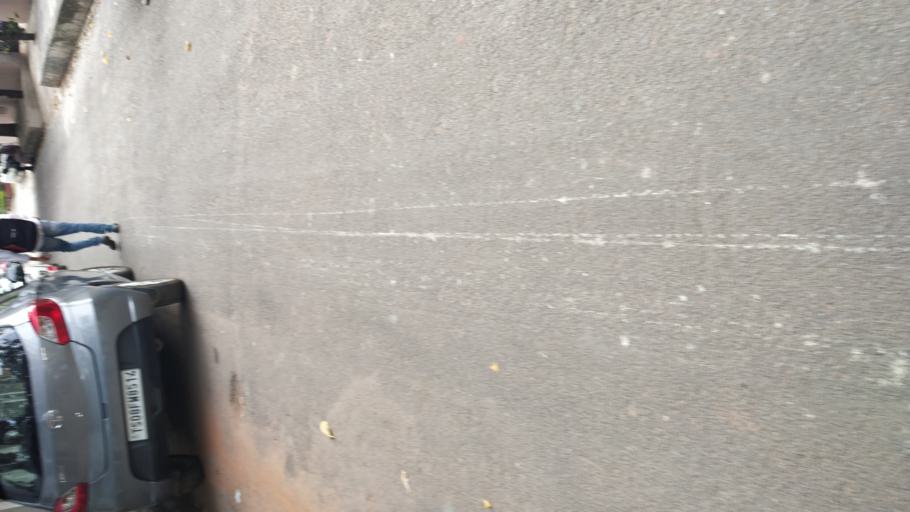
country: IN
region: Telangana
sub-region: Hyderabad
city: Hyderabad
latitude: 17.4342
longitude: 78.4513
